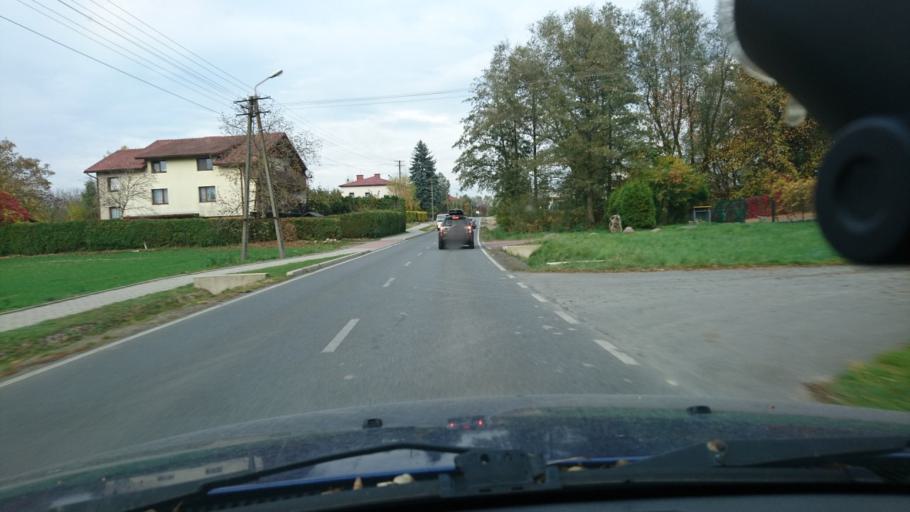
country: PL
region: Silesian Voivodeship
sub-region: Powiat bielski
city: Kozy
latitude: 49.8606
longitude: 19.1547
